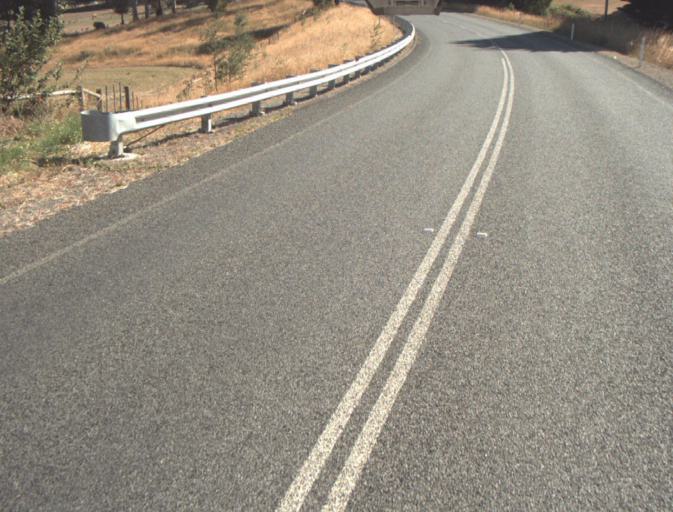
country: AU
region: Tasmania
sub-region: Dorset
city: Bridport
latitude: -41.1651
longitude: 147.2395
